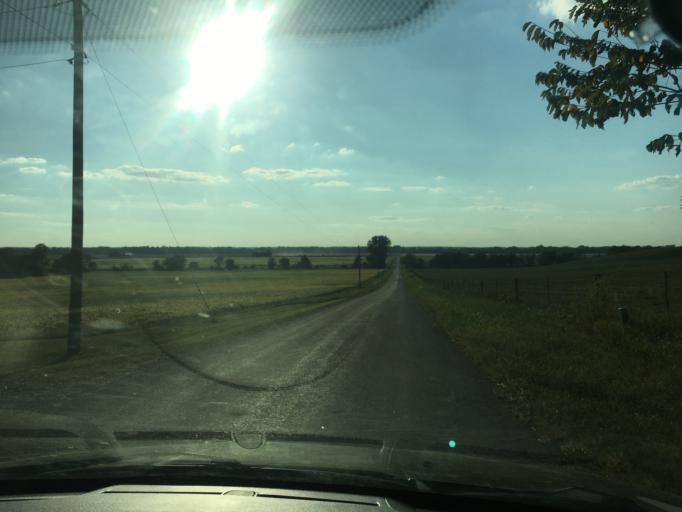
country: US
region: Ohio
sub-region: Champaign County
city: Urbana
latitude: 40.1714
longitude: -83.7689
